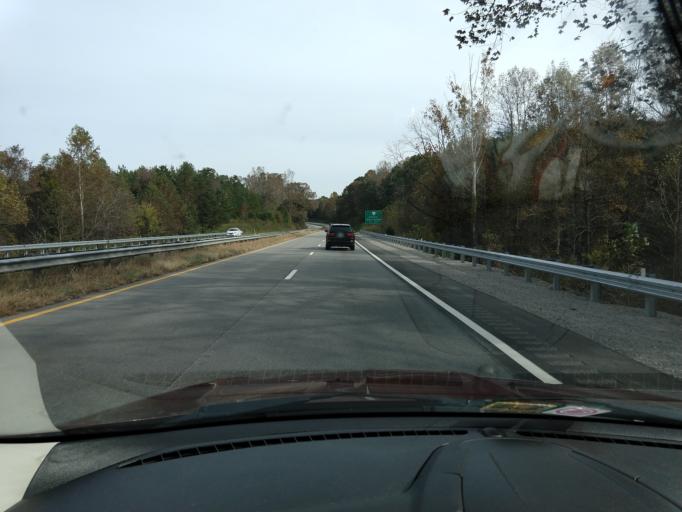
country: US
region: Virginia
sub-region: Pittsylvania County
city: Chatham
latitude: 36.8127
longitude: -79.3864
